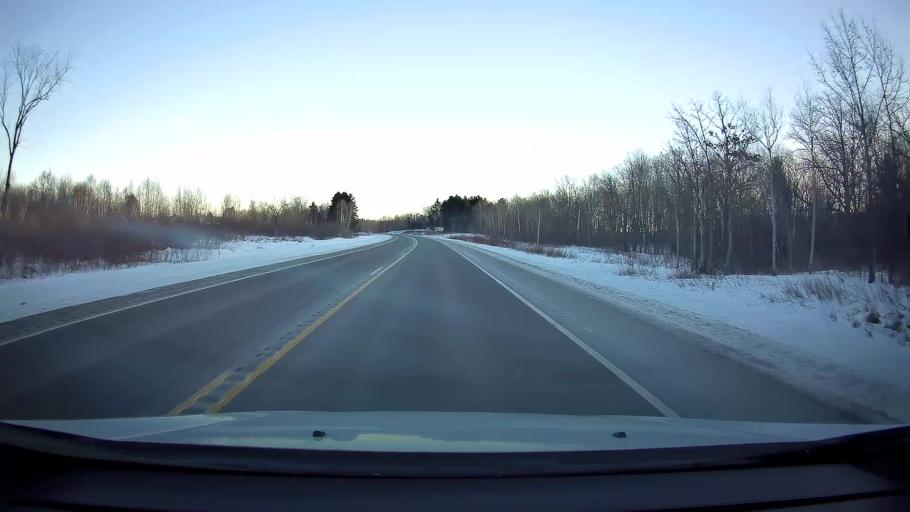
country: US
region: Wisconsin
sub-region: Washburn County
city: Shell Lake
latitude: 45.7066
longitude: -91.9482
